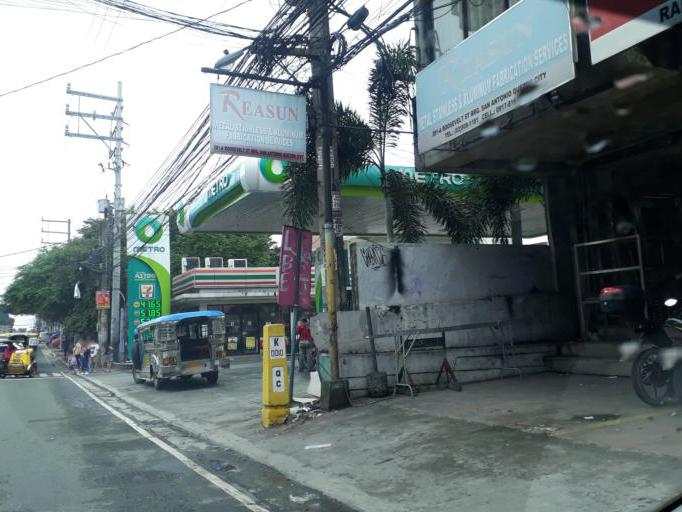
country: PH
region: Calabarzon
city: Del Monte
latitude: 14.6511
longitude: 121.0180
